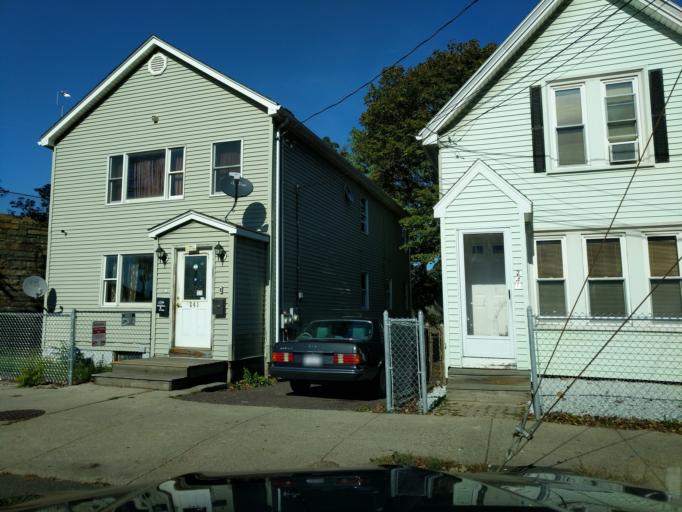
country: US
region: Massachusetts
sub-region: Suffolk County
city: Chelsea
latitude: 42.4038
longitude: -71.0288
